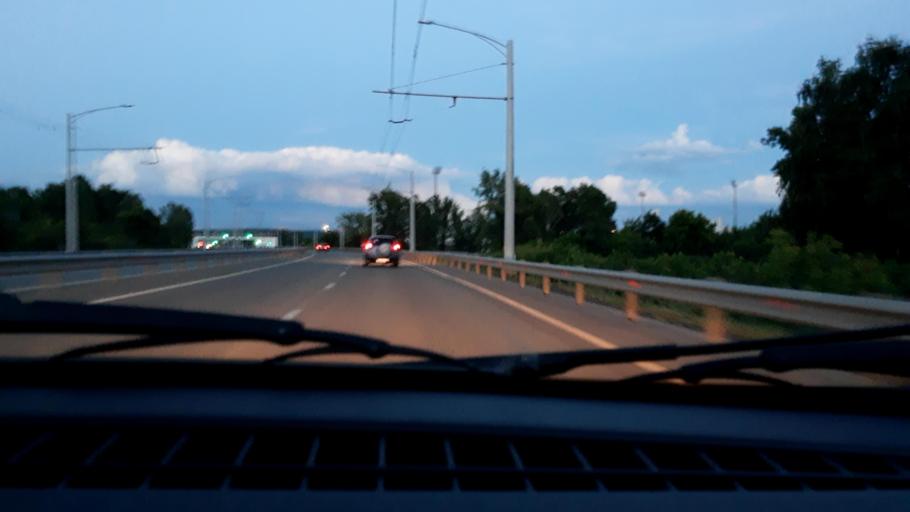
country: RU
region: Bashkortostan
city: Mikhaylovka
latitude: 54.7693
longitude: 55.9041
